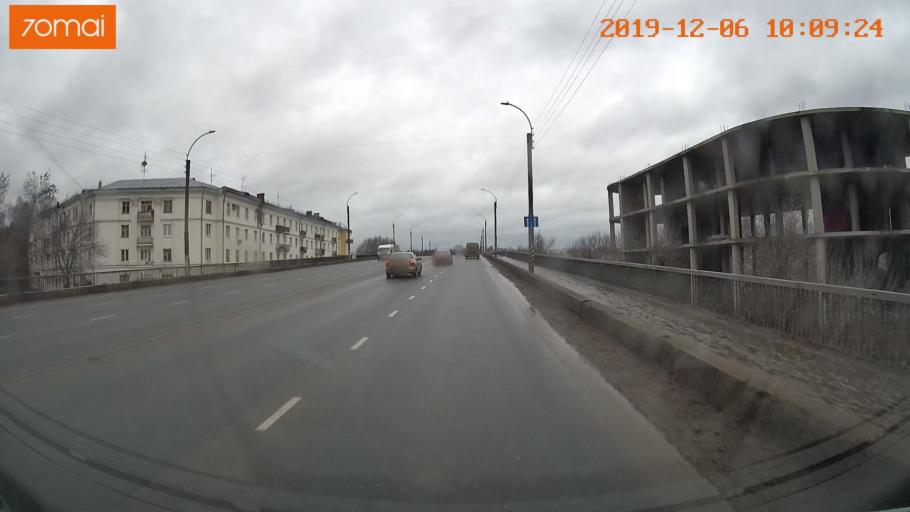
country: RU
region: Ivanovo
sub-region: Gorod Ivanovo
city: Ivanovo
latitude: 57.0231
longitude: 40.9675
